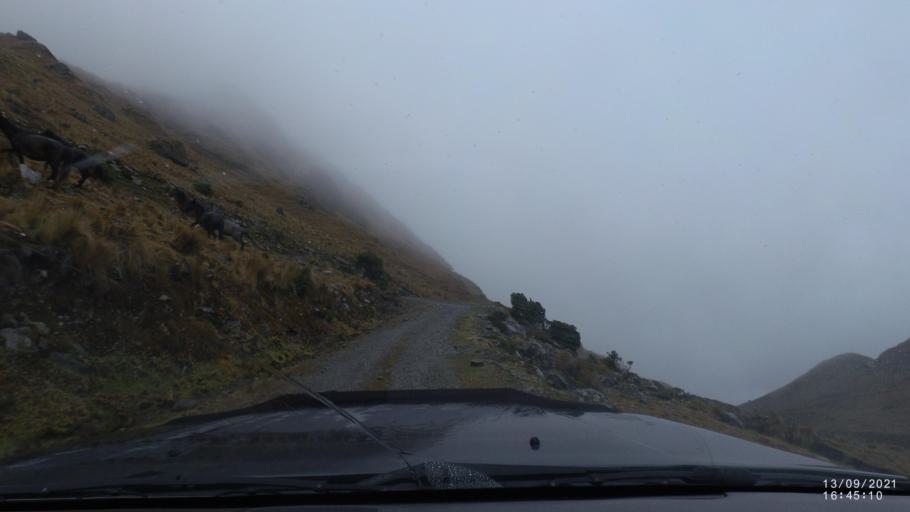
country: BO
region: Cochabamba
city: Colomi
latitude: -17.2937
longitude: -65.7111
